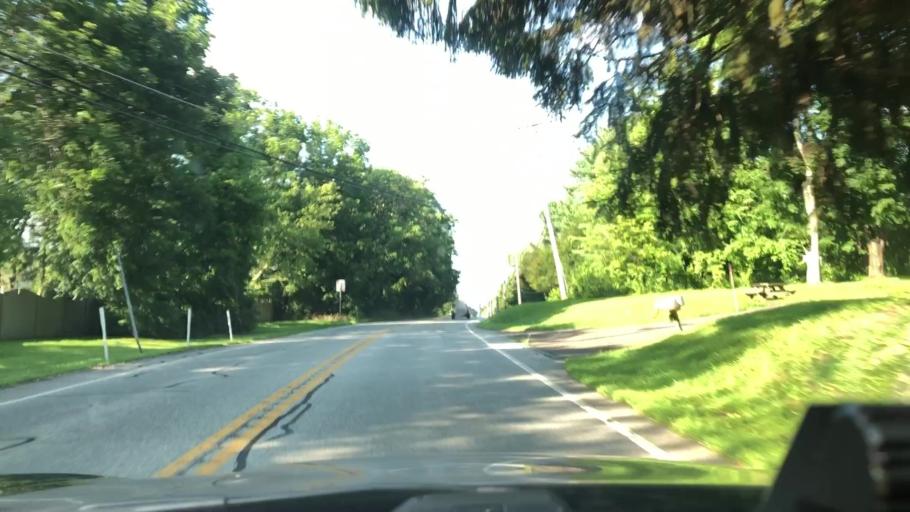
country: US
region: Pennsylvania
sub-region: Montgomery County
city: Montgomeryville
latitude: 40.2609
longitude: -75.2334
